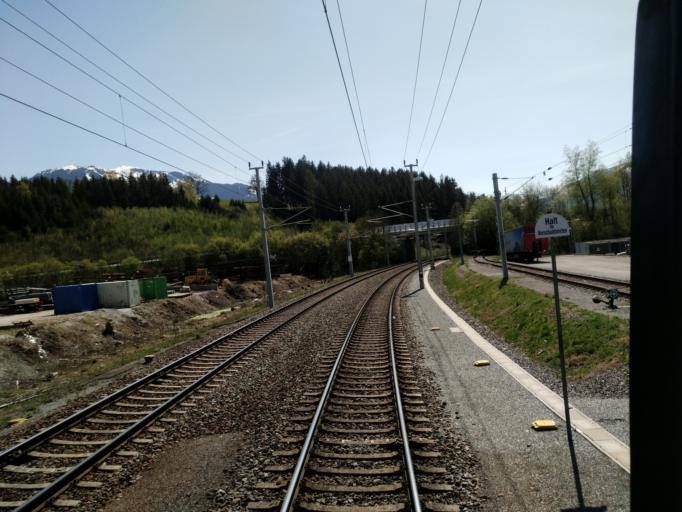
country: AT
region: Salzburg
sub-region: Politischer Bezirk Zell am See
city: Saalfelden am Steinernen Meer
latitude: 47.4208
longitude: 12.8315
